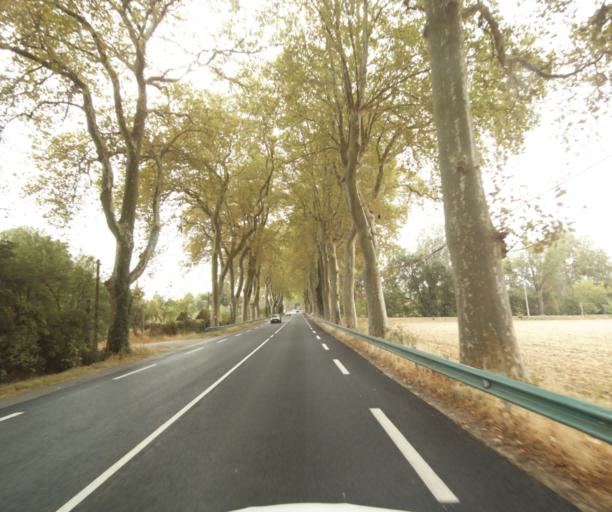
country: FR
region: Midi-Pyrenees
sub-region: Departement de la Haute-Garonne
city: Villefranche-de-Lauragais
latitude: 43.4105
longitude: 1.7051
